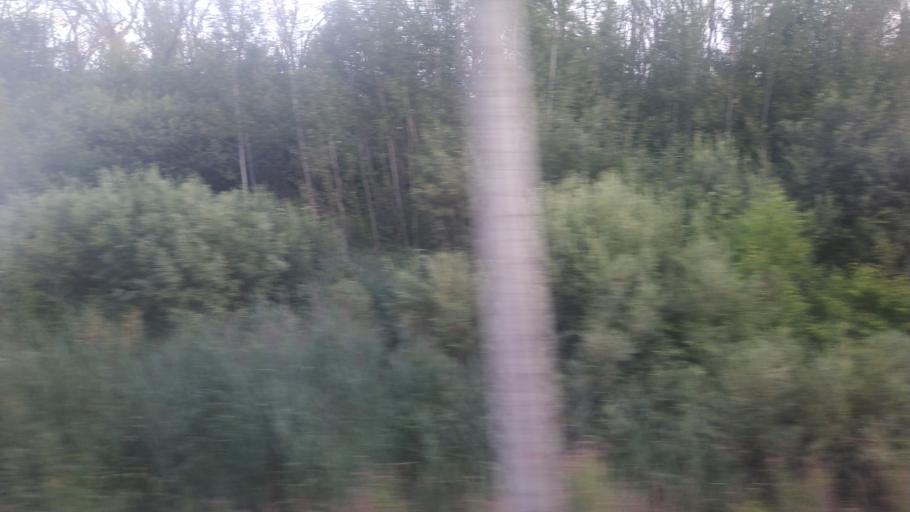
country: RU
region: Moskovskaya
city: Tugolesskiy Bor
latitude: 55.5541
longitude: 39.6985
